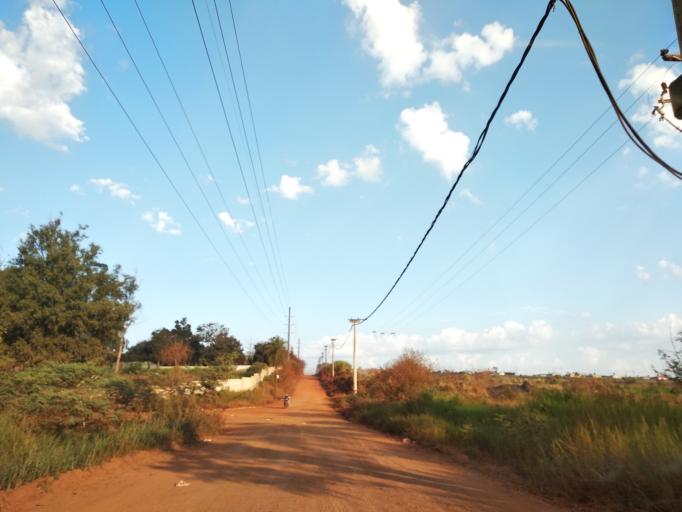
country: AR
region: Misiones
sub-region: Departamento de Capital
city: Posadas
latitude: -27.4446
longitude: -55.9197
